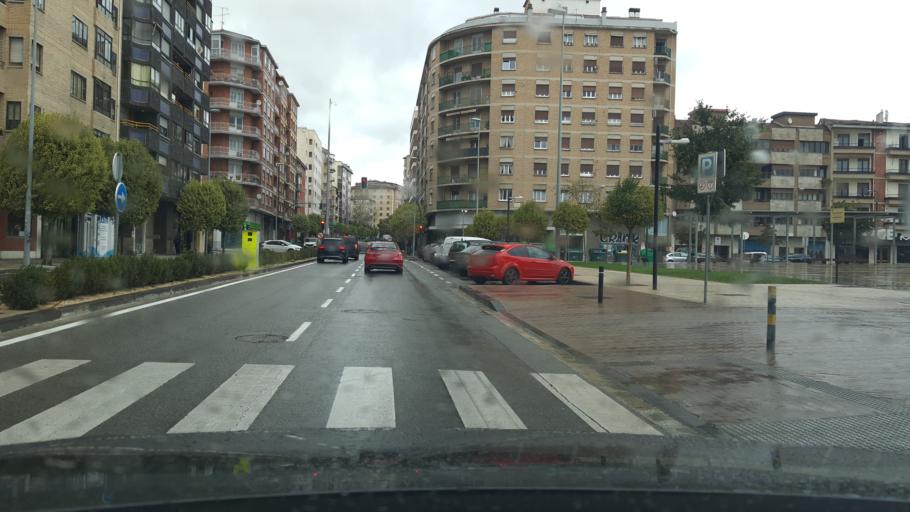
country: ES
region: Navarre
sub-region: Provincia de Navarra
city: Segundo Ensanche
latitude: 42.8020
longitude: -1.6438
